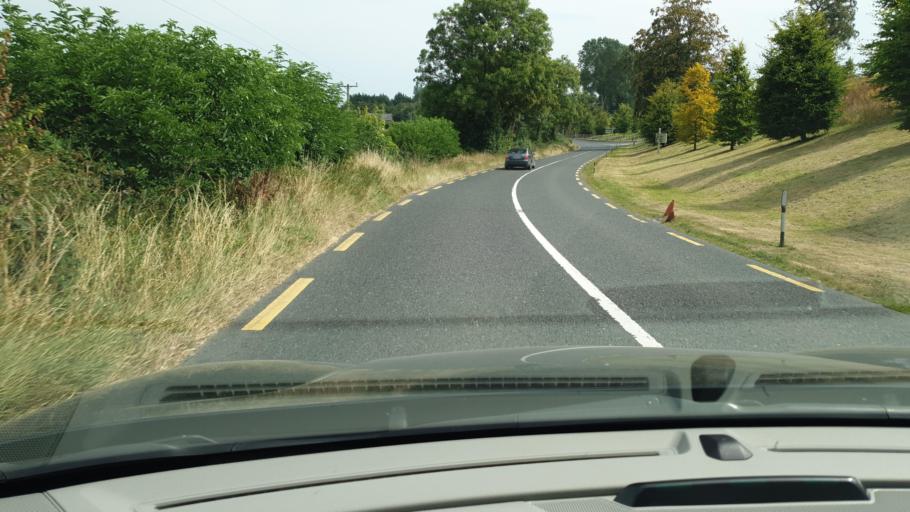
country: IE
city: Kentstown
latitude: 53.6229
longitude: -6.4934
